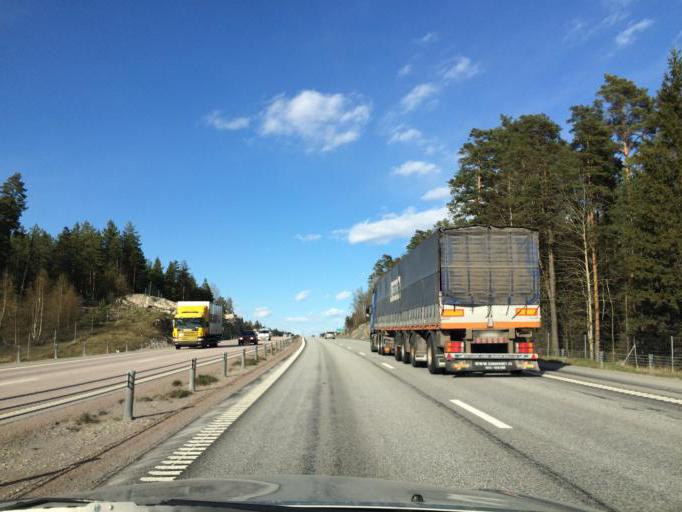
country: SE
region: Vaestmanland
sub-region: Vasteras
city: Skultuna
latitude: 59.5947
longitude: 16.4281
